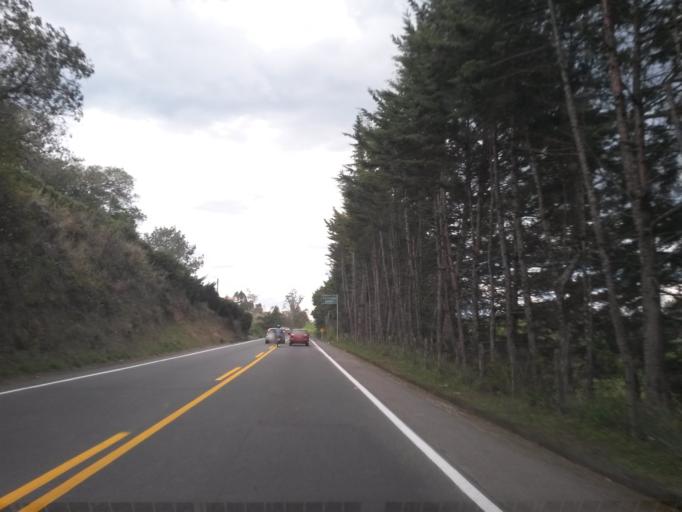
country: CO
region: Cauca
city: Popayan
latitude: 2.3645
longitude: -76.6821
